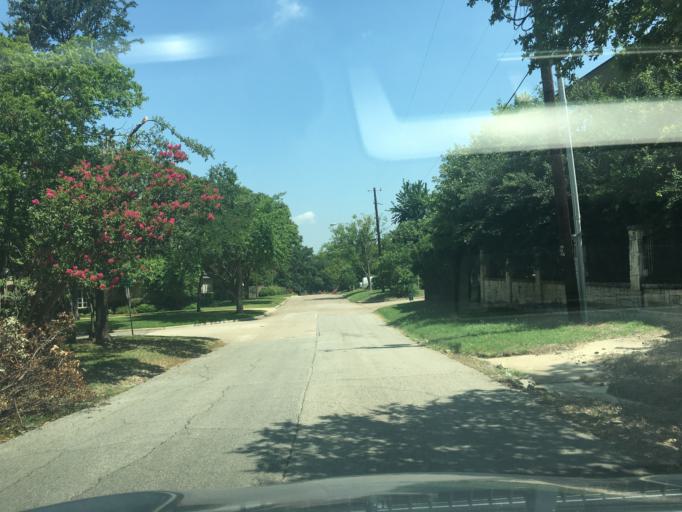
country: US
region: Texas
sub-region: Dallas County
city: Addison
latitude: 32.9187
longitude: -96.7947
